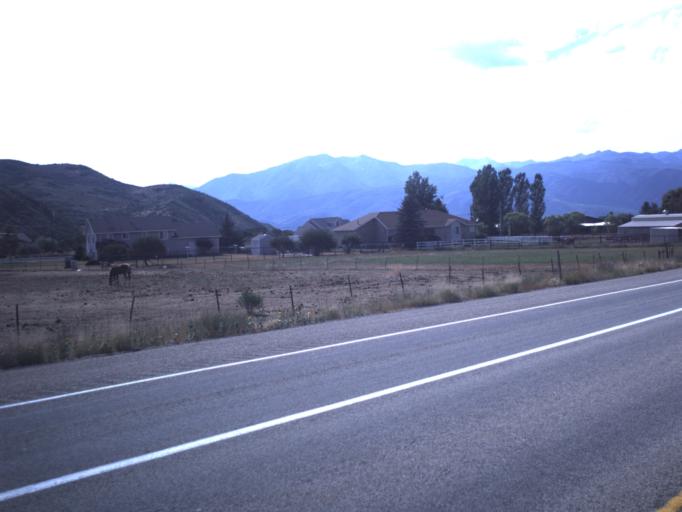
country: US
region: Utah
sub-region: Wasatch County
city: Heber
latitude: 40.4591
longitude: -111.3787
